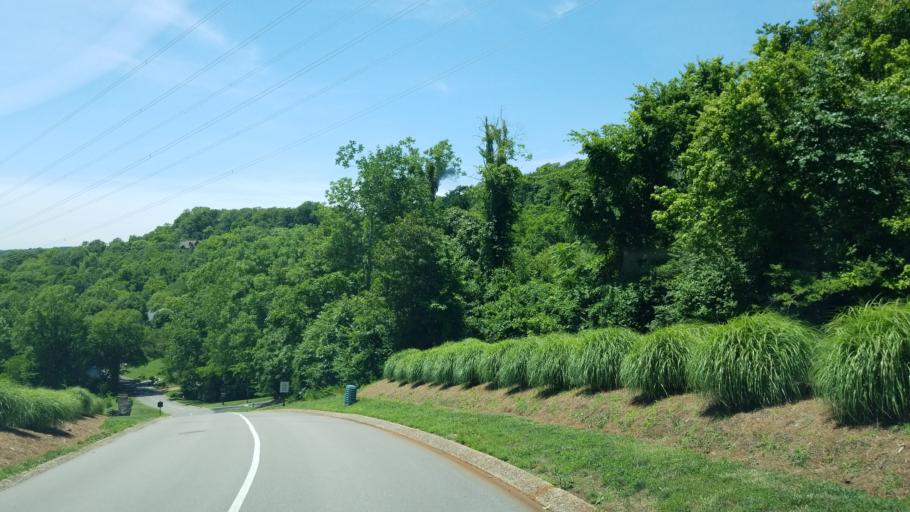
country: US
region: Tennessee
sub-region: Davidson County
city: Forest Hills
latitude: 36.0542
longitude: -86.8228
